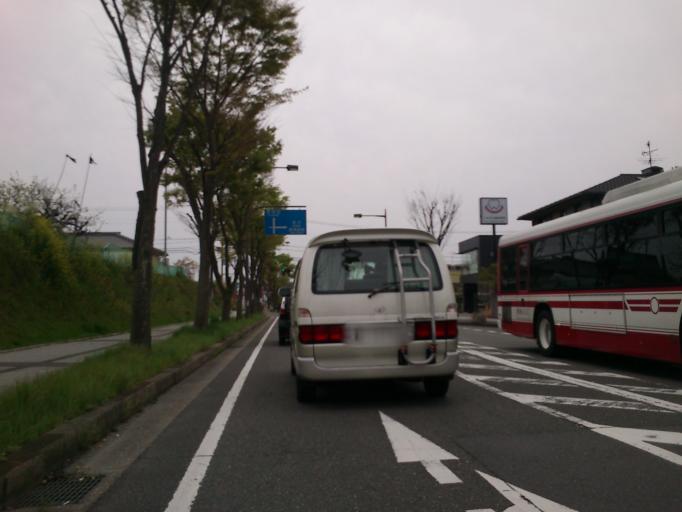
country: JP
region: Kyoto
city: Yawata
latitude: 34.8462
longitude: 135.7129
